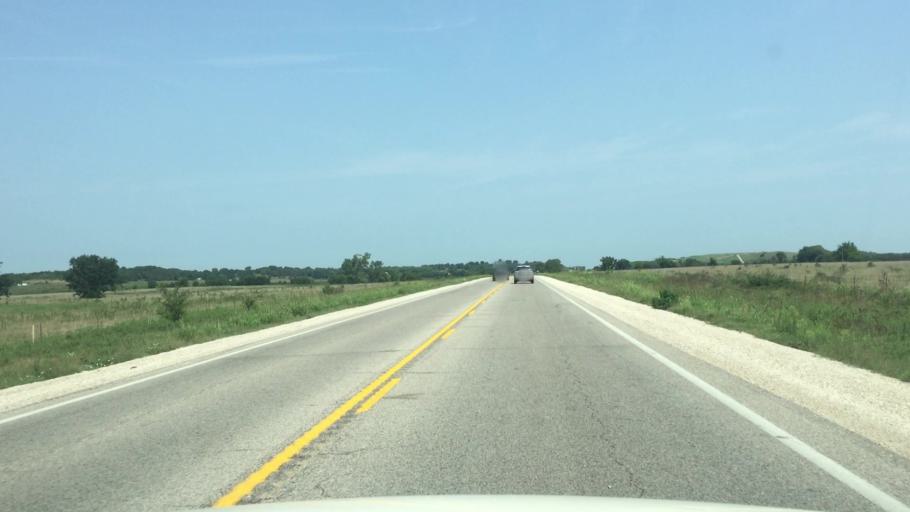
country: US
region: Kansas
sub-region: Montgomery County
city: Cherryvale
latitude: 37.1899
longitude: -95.5802
